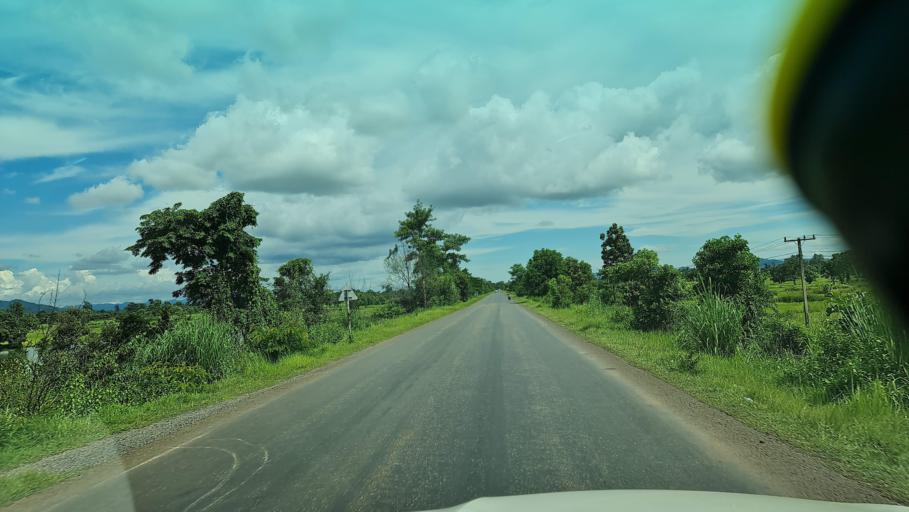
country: LA
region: Bolikhamxai
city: Ban Nahin
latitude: 18.2083
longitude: 104.2095
